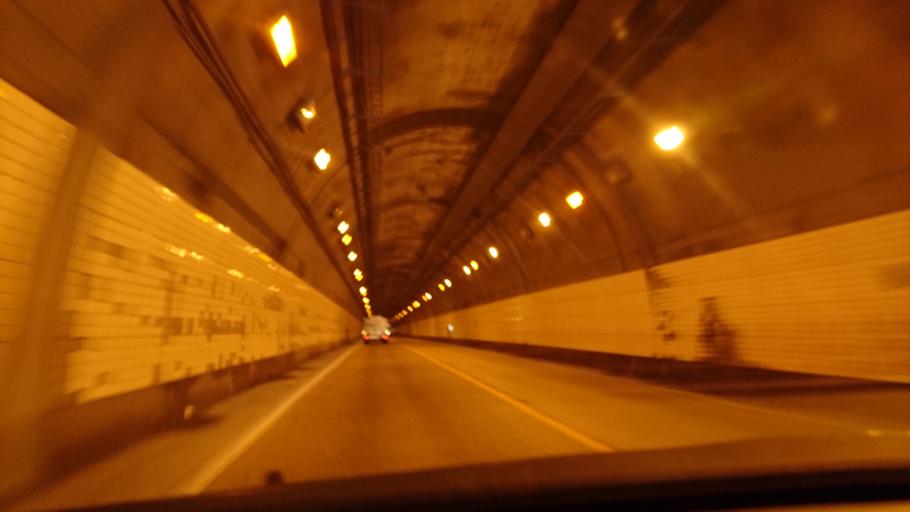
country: JP
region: Iwate
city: Kamaishi
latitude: 39.2313
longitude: 141.8833
